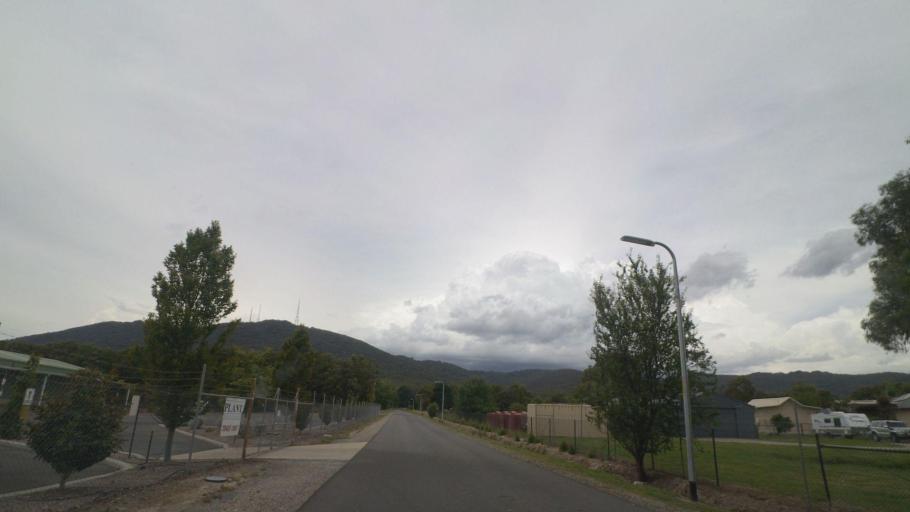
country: AU
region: Victoria
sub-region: Knox
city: The Basin
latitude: -37.8404
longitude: 145.3189
